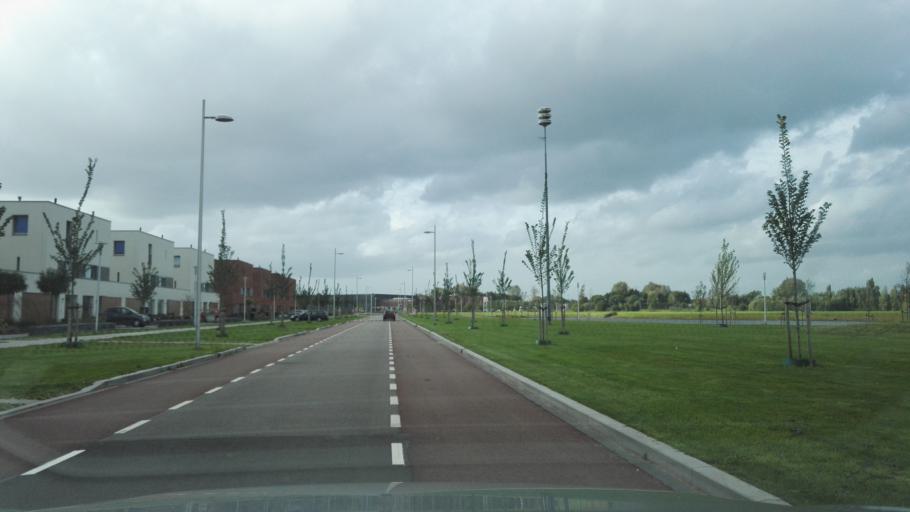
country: NL
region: Gelderland
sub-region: Gemeente Apeldoorn
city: Apeldoorn
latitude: 52.2423
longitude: 5.9966
